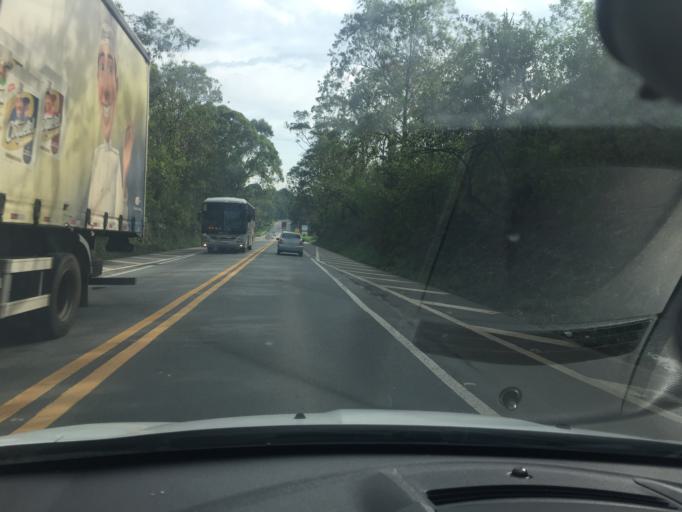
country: BR
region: Sao Paulo
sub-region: Campo Limpo Paulista
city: Campo Limpo Paulista
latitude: -23.1771
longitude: -46.7755
